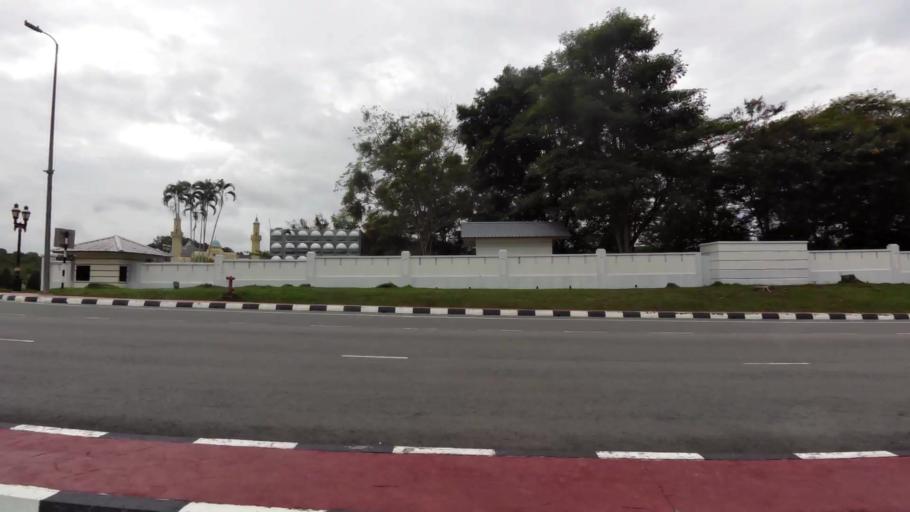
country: BN
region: Brunei and Muara
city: Bandar Seri Begawan
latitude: 4.9186
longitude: 114.9341
